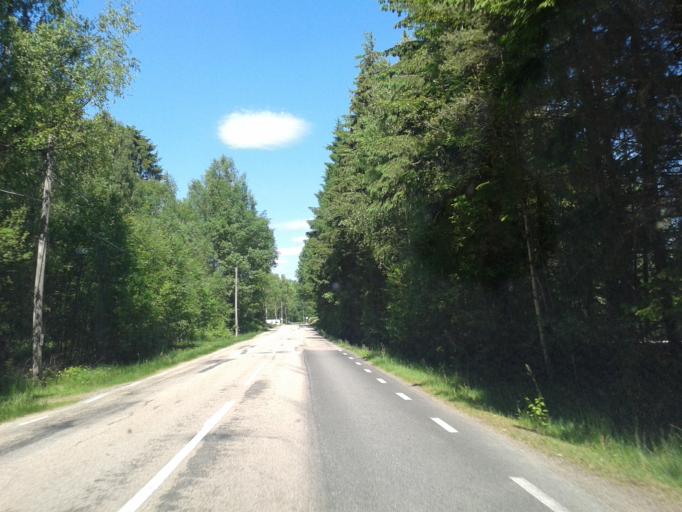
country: SE
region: Vaestra Goetaland
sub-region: Orust
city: Henan
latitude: 58.2788
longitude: 11.7172
